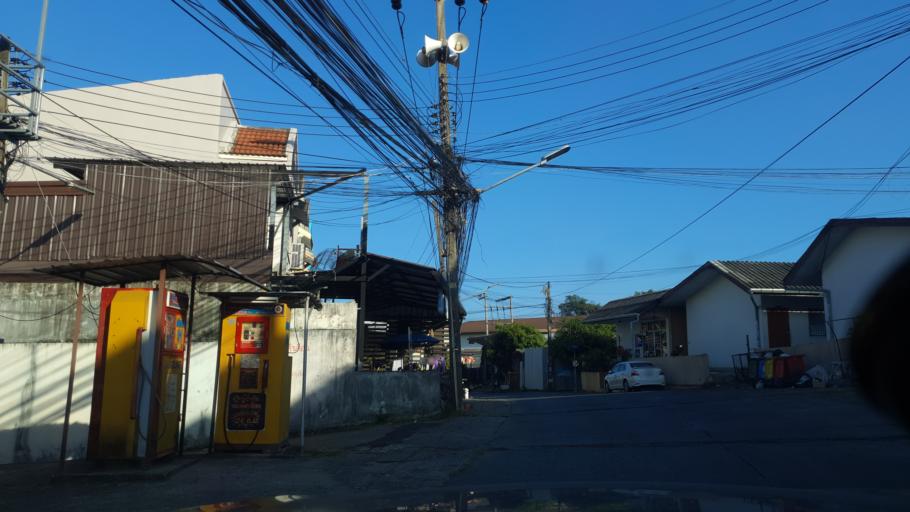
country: TH
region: Phuket
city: Kathu
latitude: 7.9028
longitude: 98.3316
